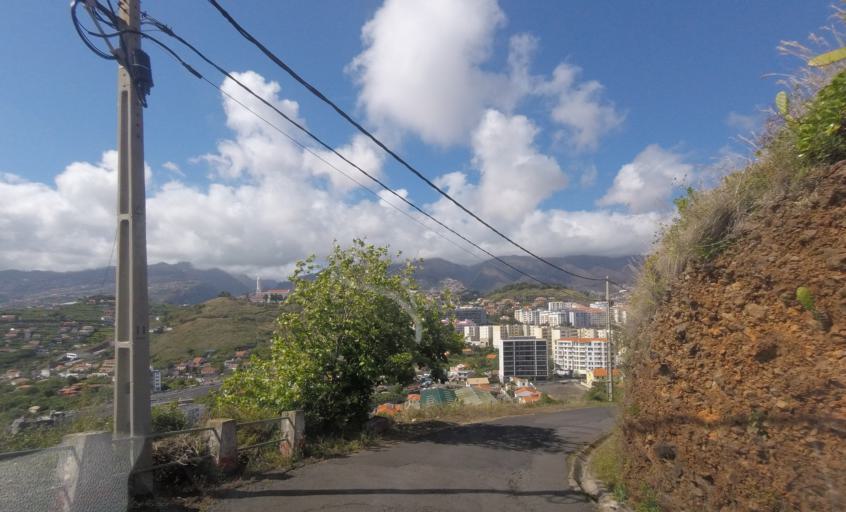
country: PT
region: Madeira
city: Camara de Lobos
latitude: 32.6429
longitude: -16.9412
